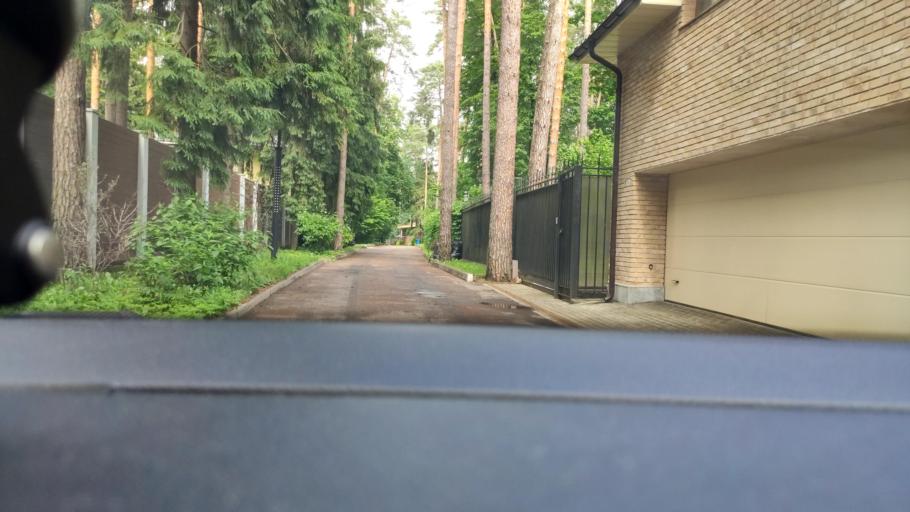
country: RU
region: Moskovskaya
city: Nikolina Gora
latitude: 55.7330
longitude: 37.0739
